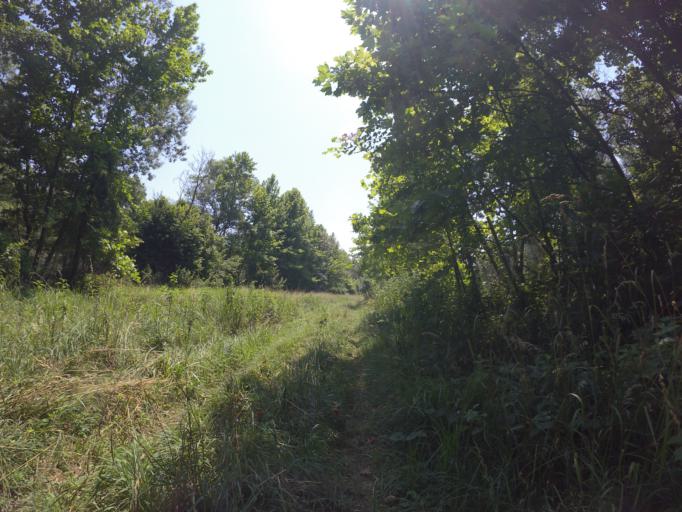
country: IT
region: Friuli Venezia Giulia
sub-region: Provincia di Udine
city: Rivignano
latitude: 45.8949
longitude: 13.0397
